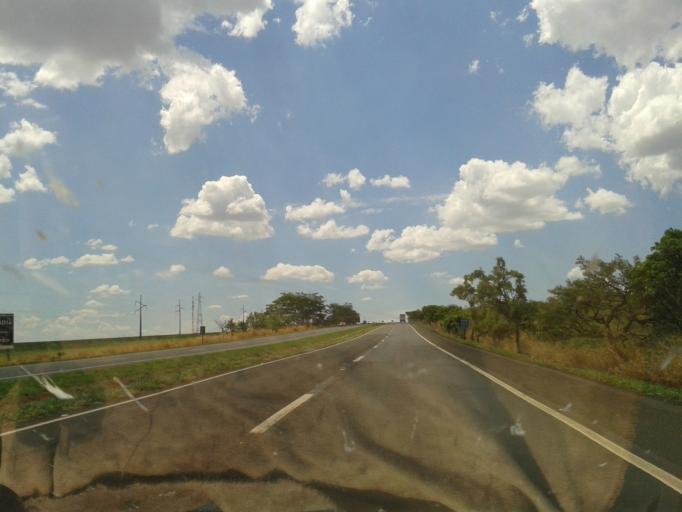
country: BR
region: Minas Gerais
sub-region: Uberlandia
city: Uberlandia
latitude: -19.0859
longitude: -48.1859
